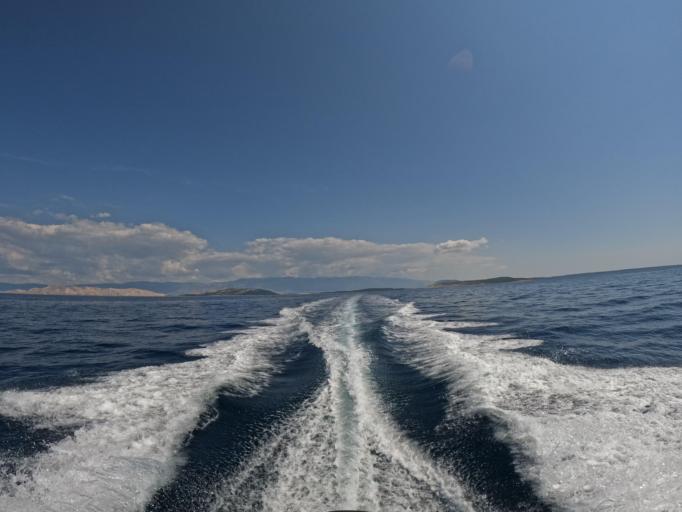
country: HR
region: Primorsko-Goranska
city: Lopar
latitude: 44.8789
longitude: 14.6545
